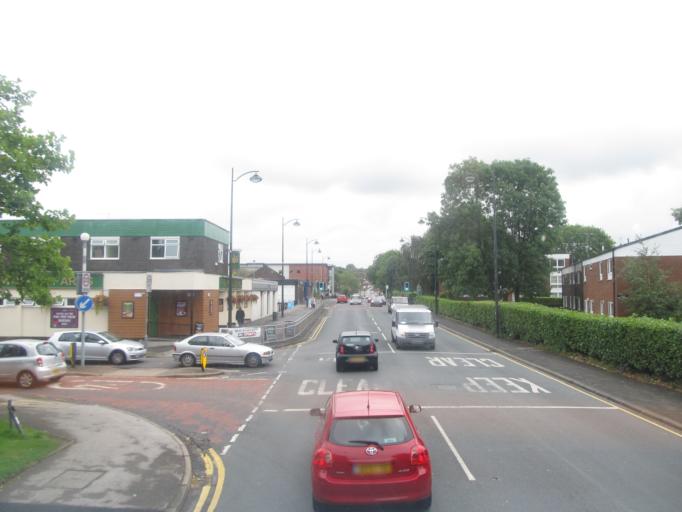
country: GB
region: England
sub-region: Borough of Tameside
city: Haughton Green
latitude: 53.4251
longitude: -2.1022
